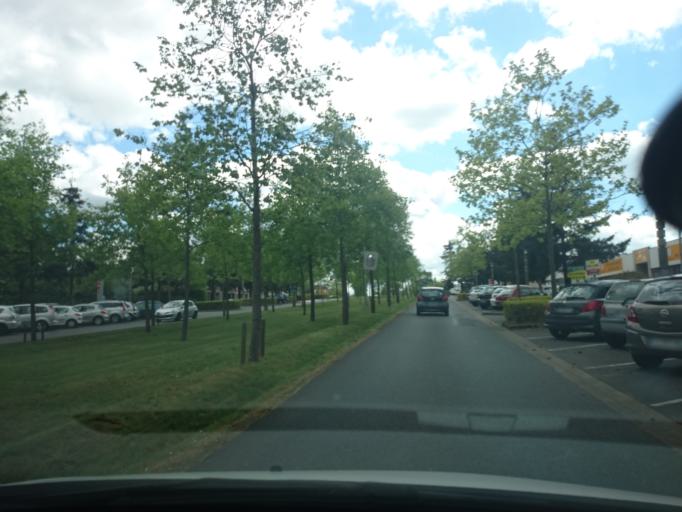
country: FR
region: Pays de la Loire
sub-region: Departement de la Loire-Atlantique
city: Saint-Herblain
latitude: 47.2246
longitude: -1.6362
